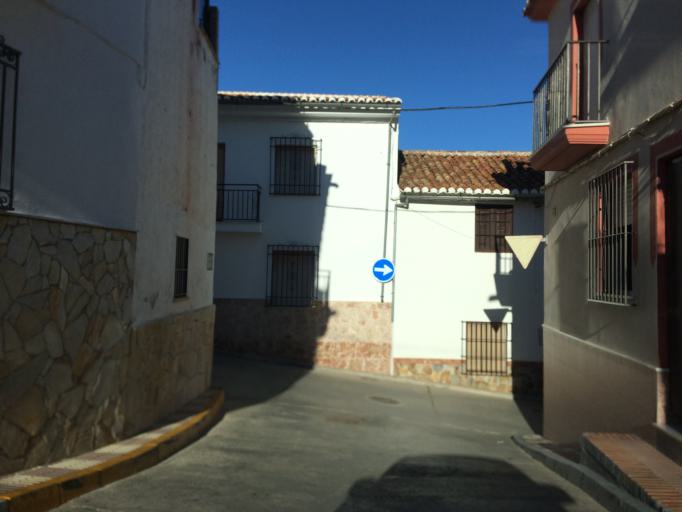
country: ES
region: Andalusia
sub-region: Provincia de Malaga
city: Casabermeja
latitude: 36.8918
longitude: -4.4285
